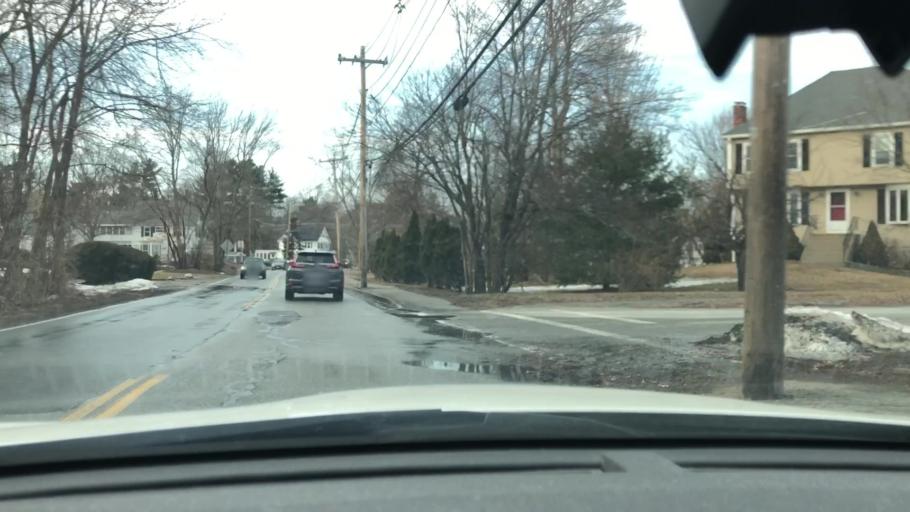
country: US
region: Massachusetts
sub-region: Middlesex County
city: Chelmsford
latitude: 42.6007
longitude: -71.3410
